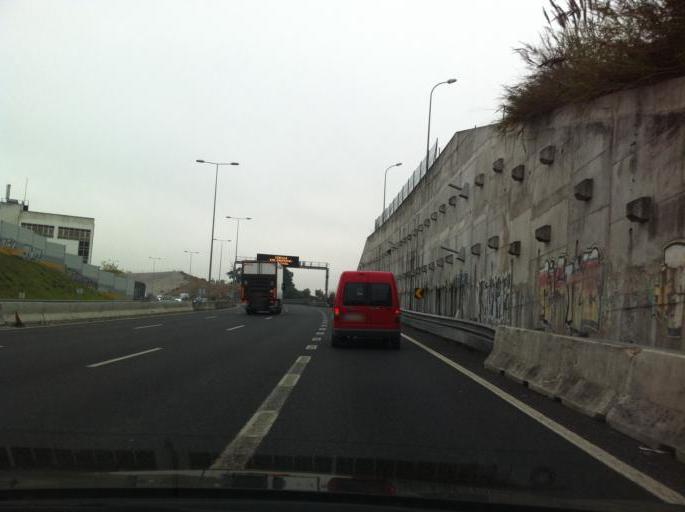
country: PT
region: Lisbon
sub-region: Odivelas
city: Pontinha
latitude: 38.7660
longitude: -9.2104
